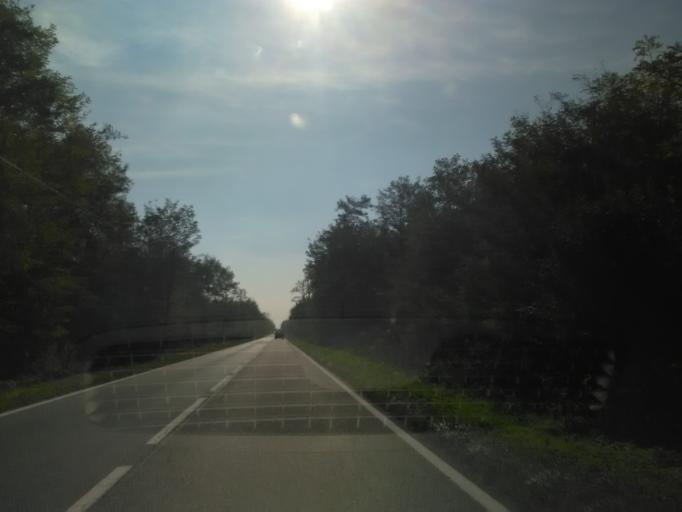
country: IT
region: Piedmont
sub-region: Provincia di Vercelli
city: Gattinara
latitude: 45.5911
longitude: 8.3714
